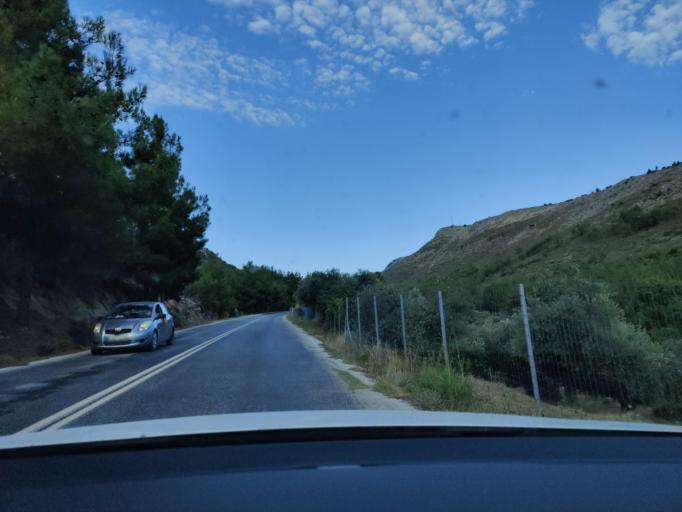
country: GR
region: East Macedonia and Thrace
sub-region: Nomos Kavalas
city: Limenaria
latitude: 40.6170
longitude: 24.6415
